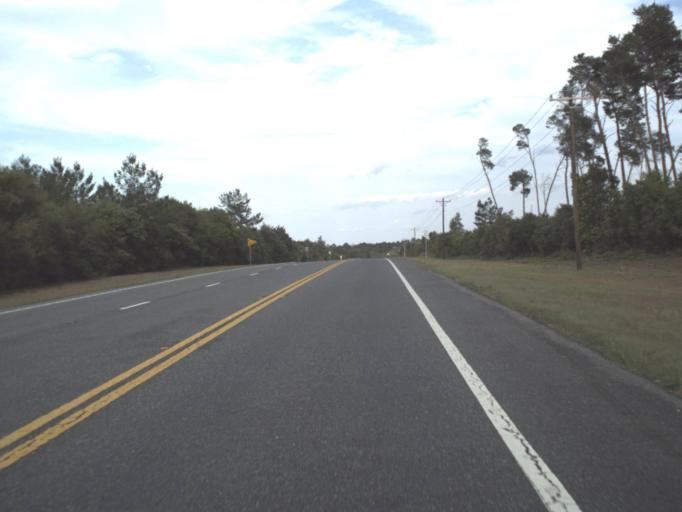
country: US
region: Florida
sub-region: Lake County
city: Astor
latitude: 29.1781
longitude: -81.7183
